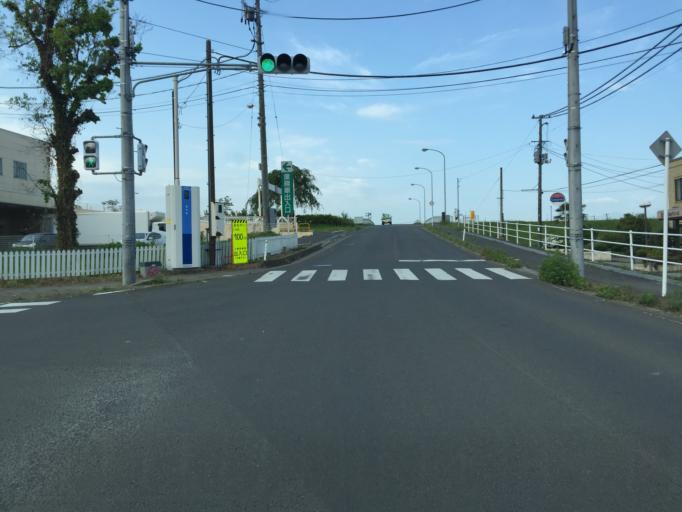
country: JP
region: Fukushima
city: Yanagawamachi-saiwaicho
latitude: 37.8574
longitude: 140.6063
